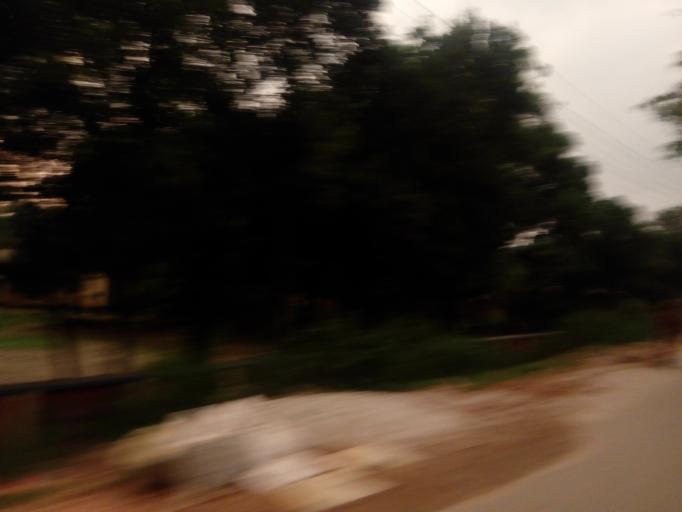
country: BD
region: Rajshahi
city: Sirajganj
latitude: 24.3016
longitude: 89.6974
